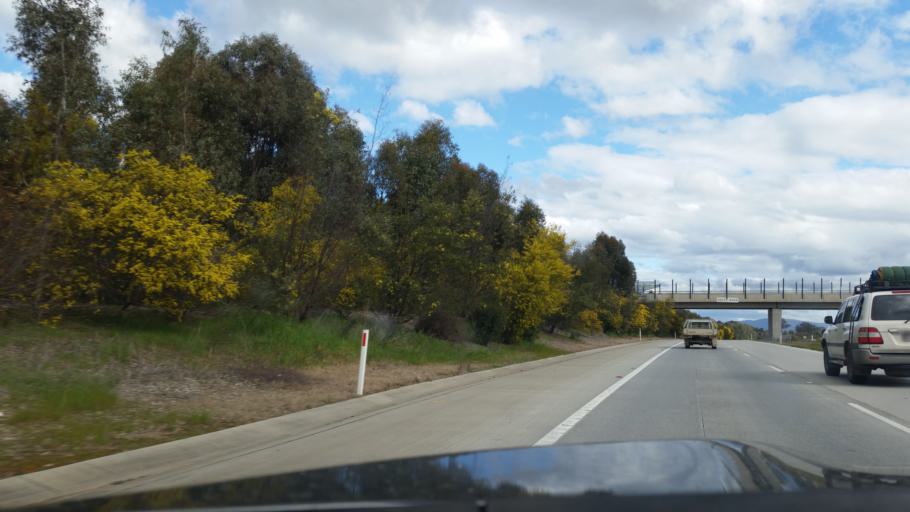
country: AU
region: New South Wales
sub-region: Albury Municipality
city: Lavington
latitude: -36.0005
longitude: 146.9923
